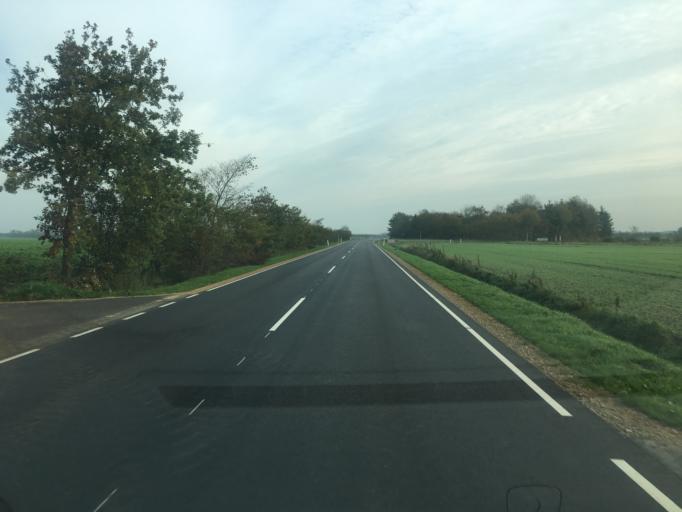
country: DK
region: South Denmark
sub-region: Tonder Kommune
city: Logumkloster
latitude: 55.0779
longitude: 8.9830
